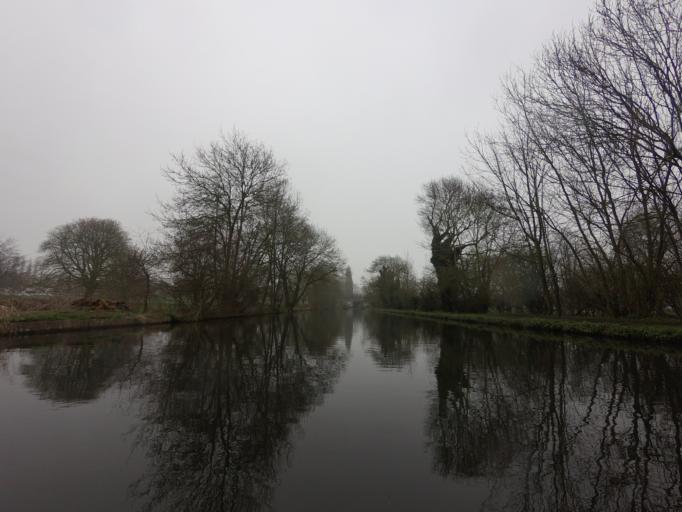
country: GB
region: England
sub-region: Hertfordshire
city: Hemel Hempstead
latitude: 51.7445
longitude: -0.4843
